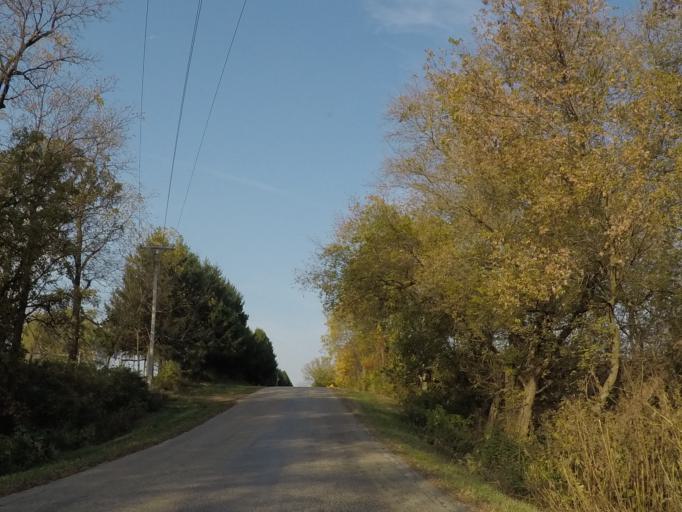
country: US
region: Wisconsin
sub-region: Dane County
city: Cross Plains
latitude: 43.0421
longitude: -89.6107
